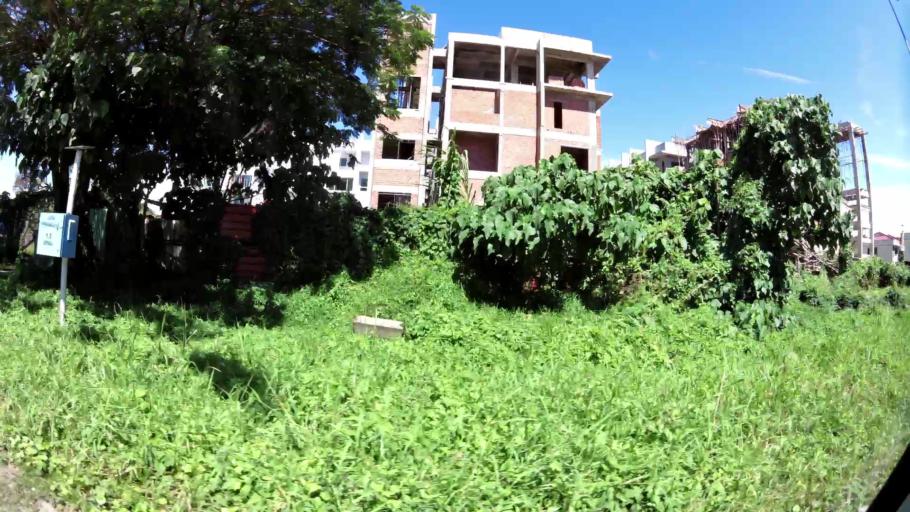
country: BN
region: Brunei and Muara
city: Bandar Seri Begawan
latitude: 5.0288
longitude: 115.0626
